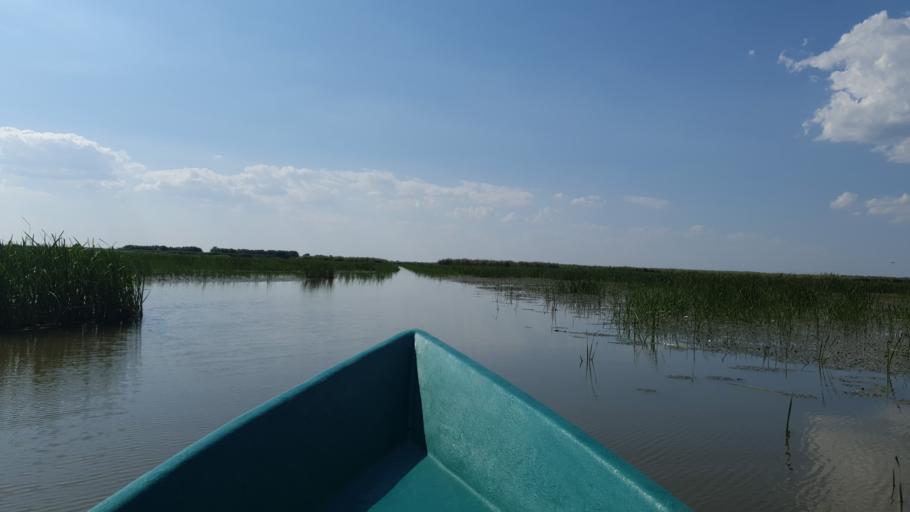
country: RU
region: Astrakhan
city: Kirovskiy
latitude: 45.8347
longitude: 48.4188
